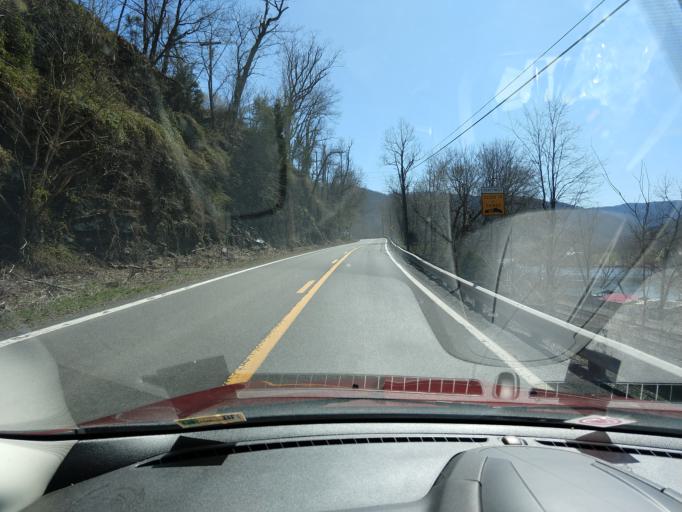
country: US
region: West Virginia
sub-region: Summers County
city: Hinton
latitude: 37.7725
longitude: -80.8911
